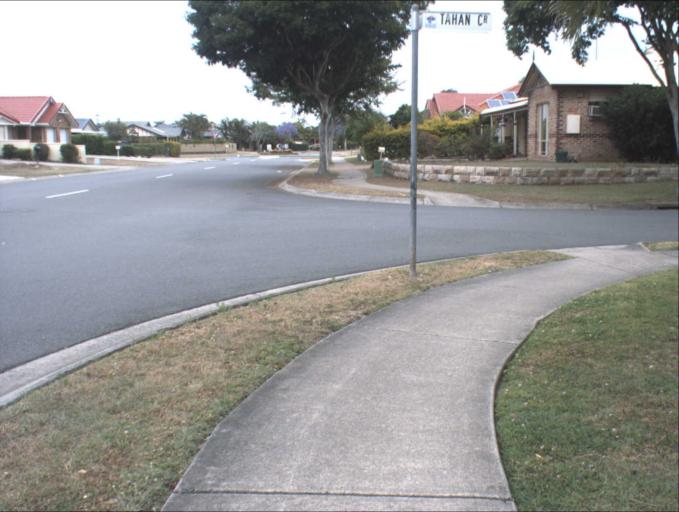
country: AU
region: Queensland
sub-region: Logan
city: Slacks Creek
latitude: -27.6782
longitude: 153.1741
